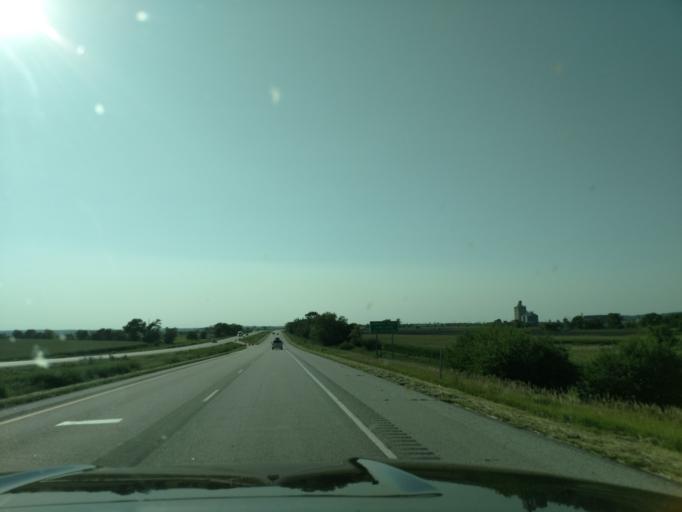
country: US
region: Iowa
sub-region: Fremont County
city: Hamburg
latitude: 40.5885
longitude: -95.6601
